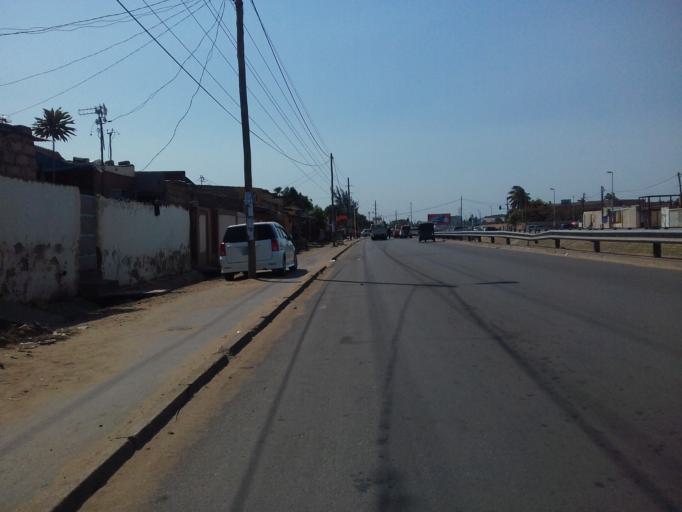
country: MZ
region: Maputo City
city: Maputo
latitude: -25.9448
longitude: 32.5744
